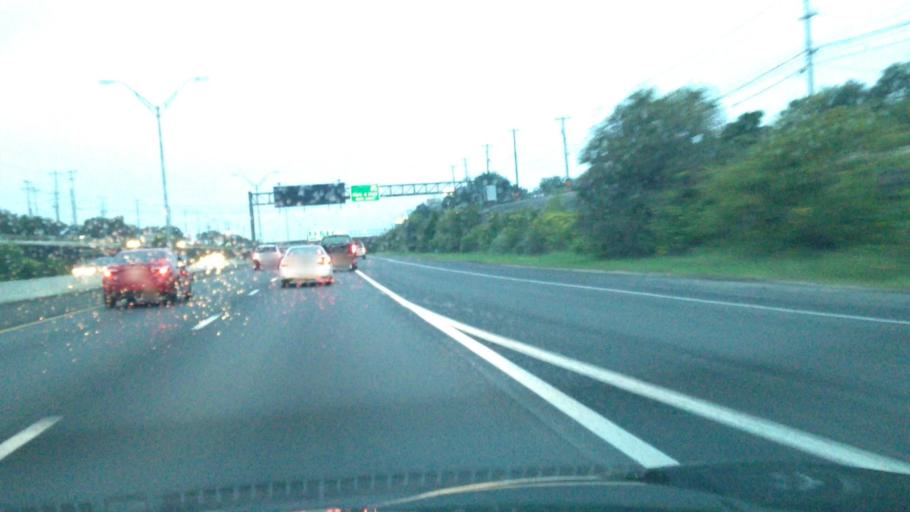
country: US
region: Texas
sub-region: Bexar County
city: Shavano Park
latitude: 29.5931
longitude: -98.5828
